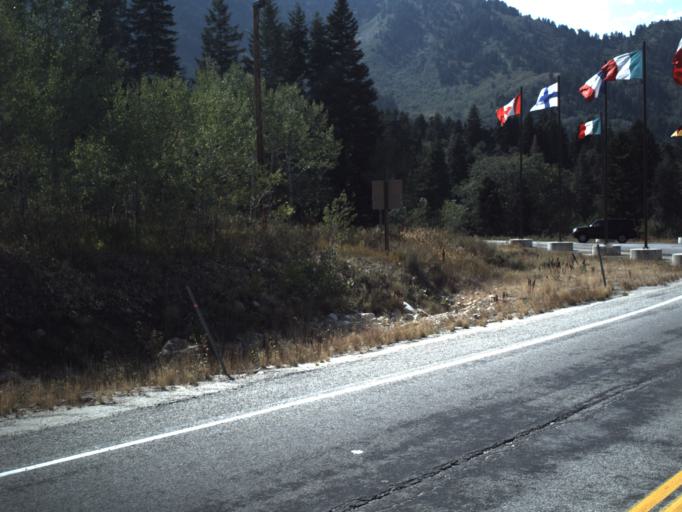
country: US
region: Utah
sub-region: Morgan County
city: Mountain Green
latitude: 41.2207
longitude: -111.8541
